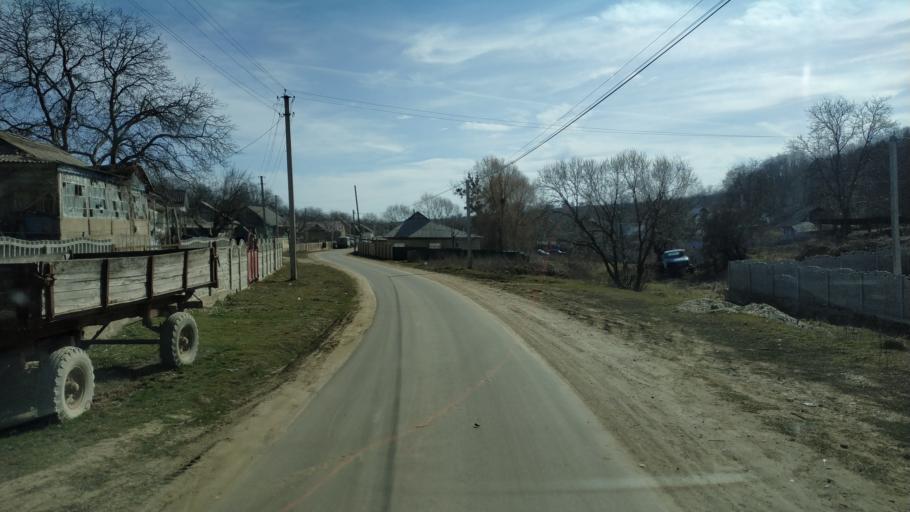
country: MD
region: Nisporeni
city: Nisporeni
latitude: 47.0971
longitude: 28.2950
